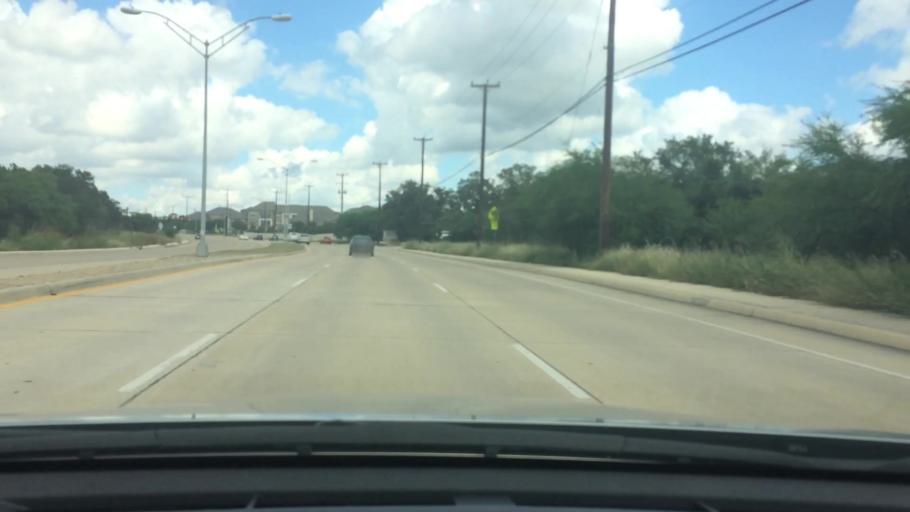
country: US
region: Texas
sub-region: Bexar County
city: Hollywood Park
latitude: 29.6279
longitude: -98.4234
